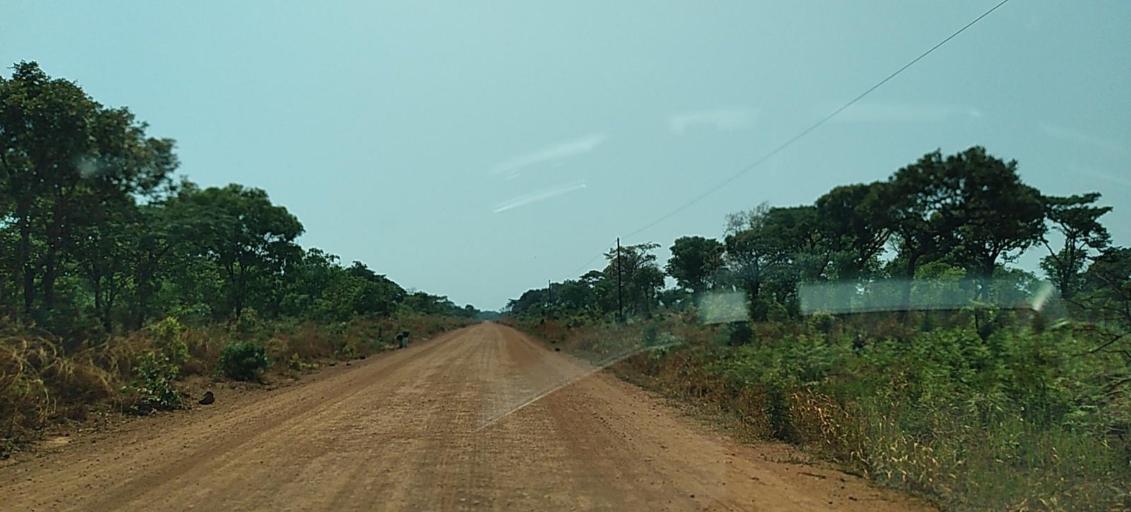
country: ZM
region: North-Western
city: Kansanshi
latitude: -11.9935
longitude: 26.6356
